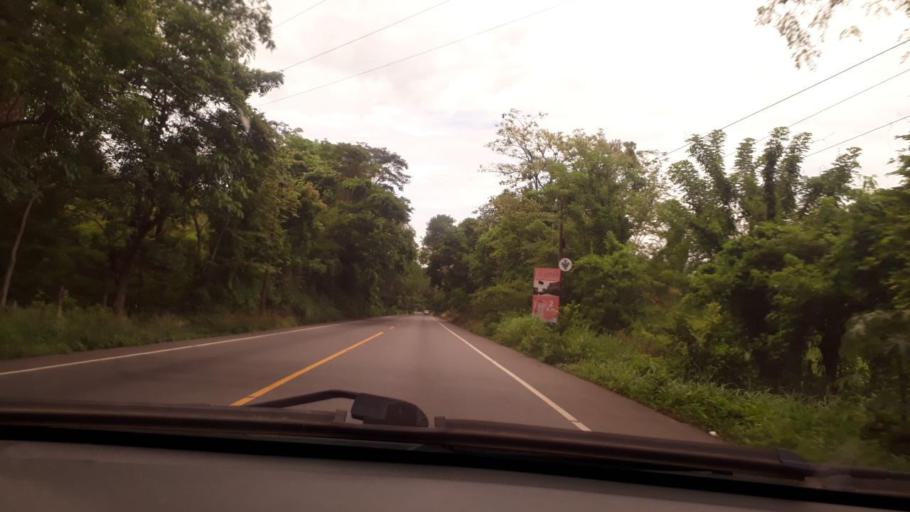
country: GT
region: Zacapa
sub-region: Municipio de Zacapa
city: Gualan
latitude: 15.1978
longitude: -89.2731
